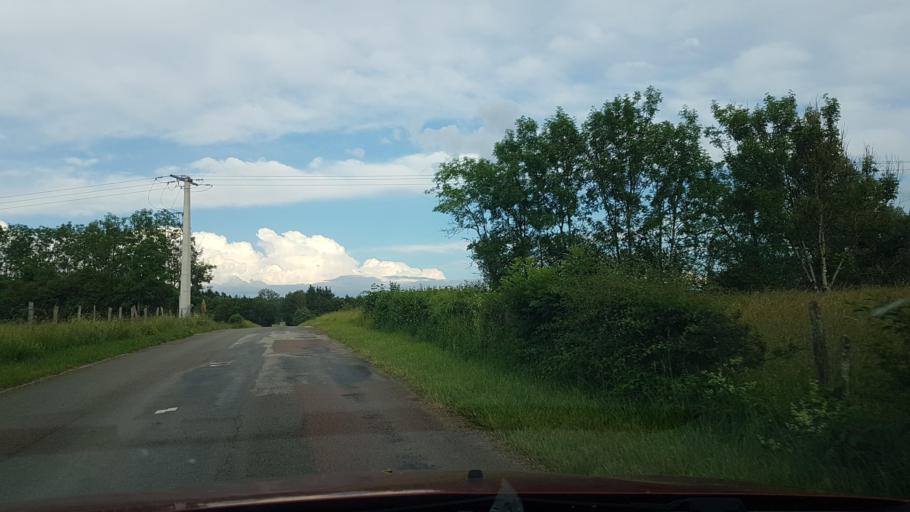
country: FR
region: Franche-Comte
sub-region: Departement du Jura
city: Clairvaux-les-Lacs
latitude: 46.5849
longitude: 5.7119
